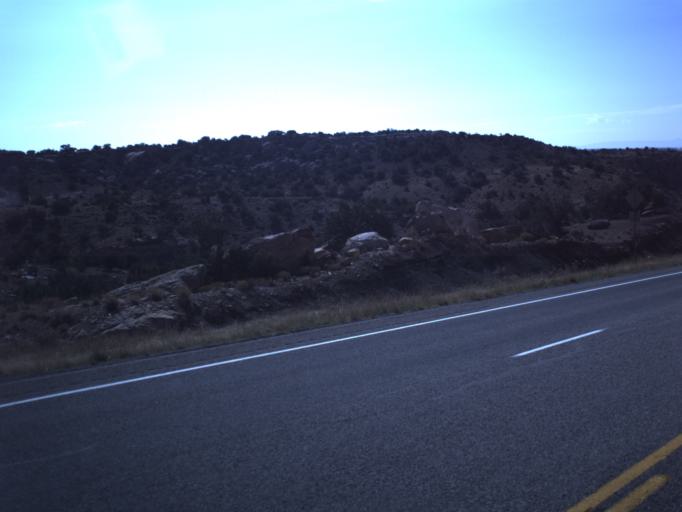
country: US
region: Utah
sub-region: San Juan County
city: Blanding
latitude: 37.4326
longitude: -109.4715
